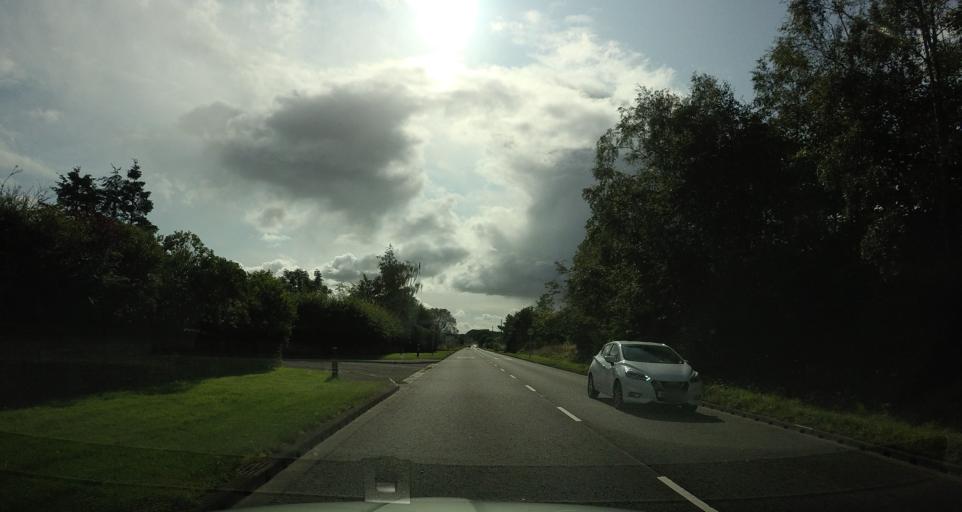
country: GB
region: Scotland
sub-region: Fife
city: Saline
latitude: 56.1880
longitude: -3.5447
